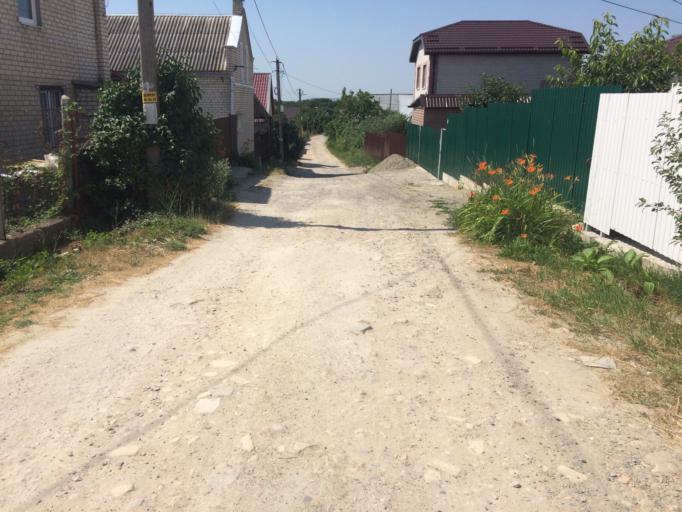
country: RU
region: Stavropol'skiy
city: Tatarka
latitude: 44.9831
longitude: 41.9413
